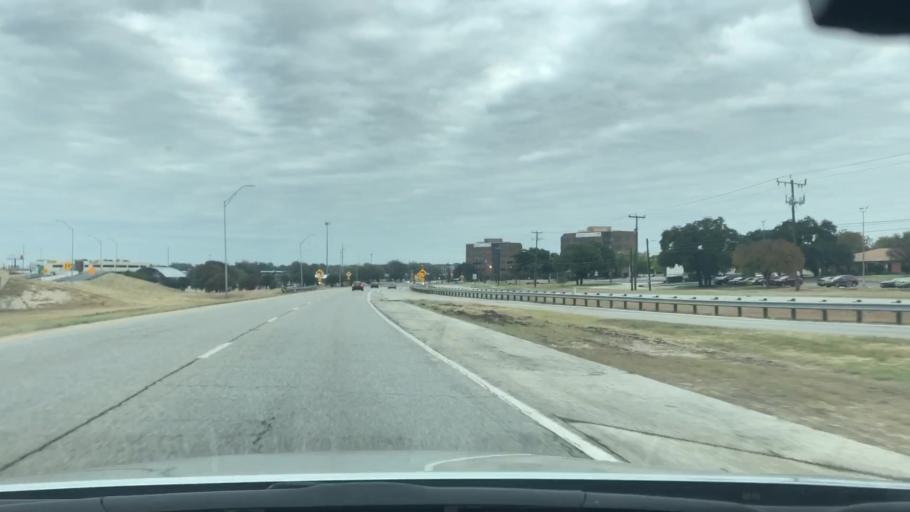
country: US
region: Texas
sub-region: Bexar County
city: Windcrest
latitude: 29.5202
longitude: -98.3943
